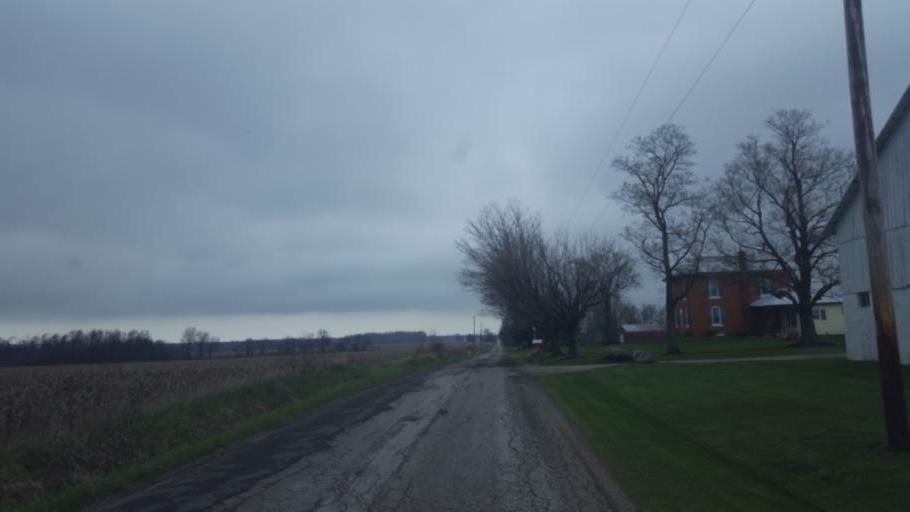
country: US
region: Ohio
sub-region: Crawford County
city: Galion
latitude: 40.6999
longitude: -82.7461
